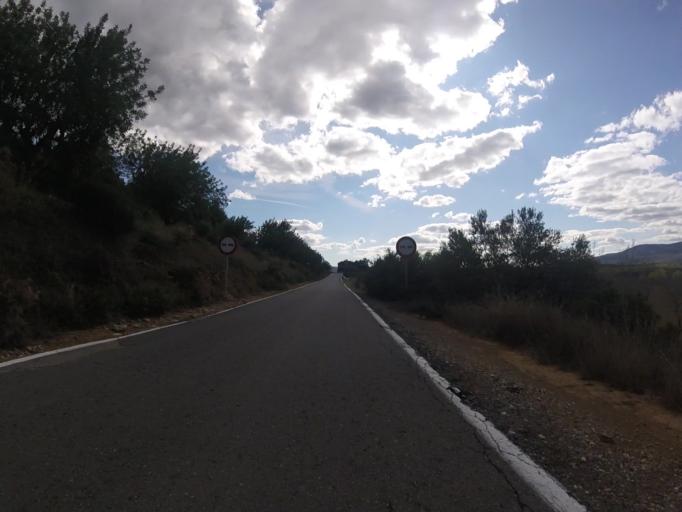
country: ES
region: Valencia
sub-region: Provincia de Castello
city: Cuevas de Vinroma
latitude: 40.3539
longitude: 0.1270
